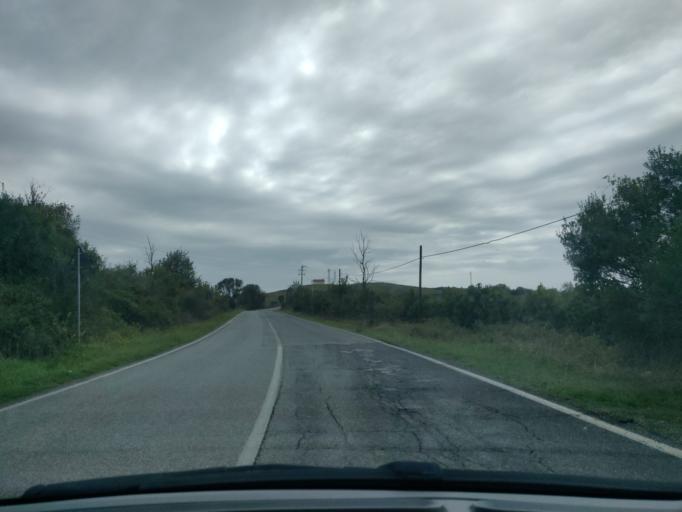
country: IT
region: Latium
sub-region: Citta metropolitana di Roma Capitale
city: Allumiere
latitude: 42.1191
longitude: 11.8615
